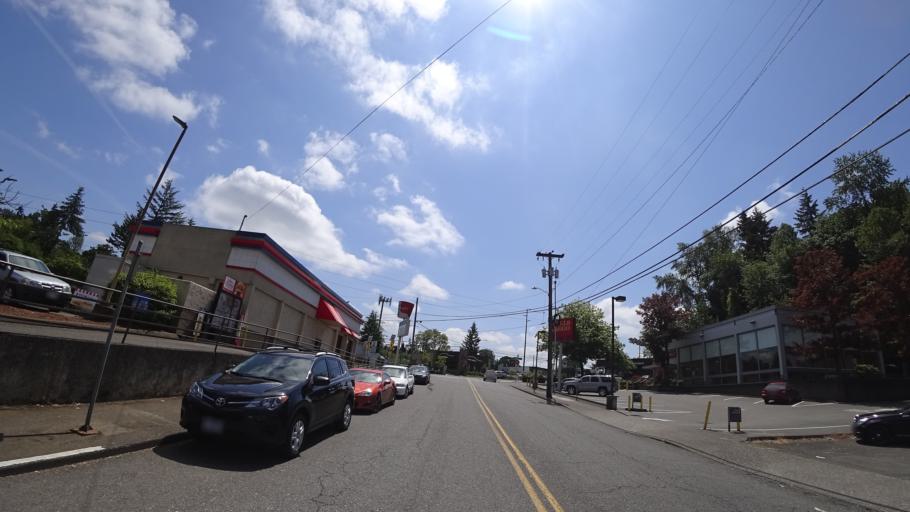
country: US
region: Oregon
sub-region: Clackamas County
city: Lake Oswego
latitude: 45.4696
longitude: -122.6921
